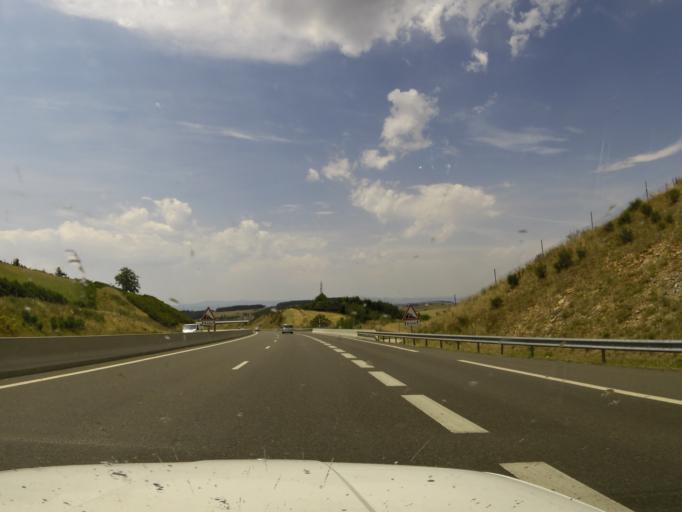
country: FR
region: Rhone-Alpes
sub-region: Departement de la Loire
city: Bussieres
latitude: 45.8709
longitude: 4.2948
